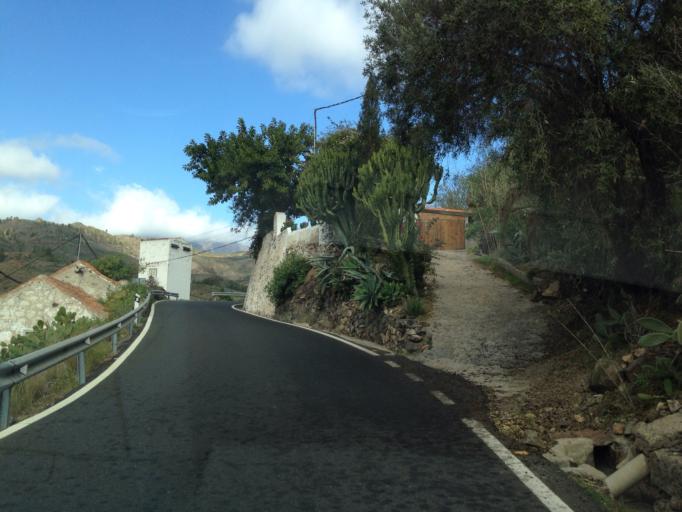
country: ES
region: Canary Islands
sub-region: Provincia de Las Palmas
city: Santa Lucia
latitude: 27.8883
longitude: -15.5632
